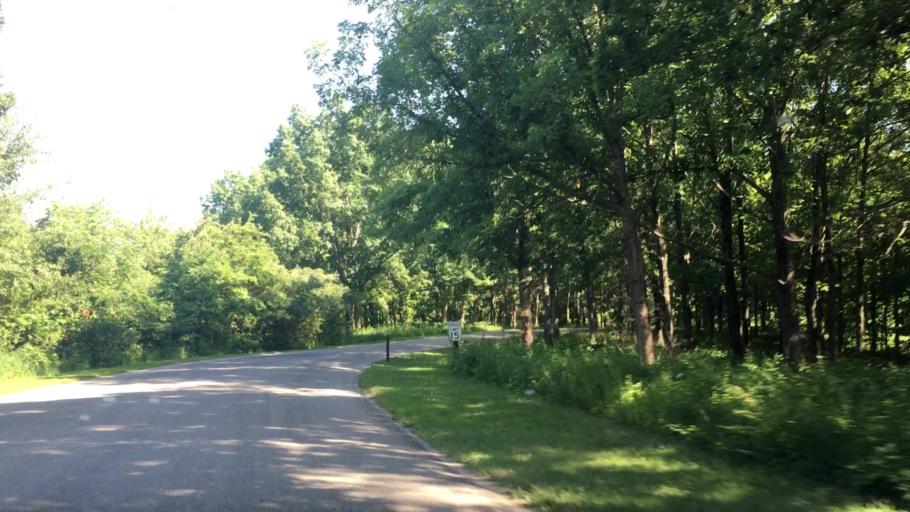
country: US
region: Iowa
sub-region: Johnson County
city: Tiffin
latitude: 41.7270
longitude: -91.7239
